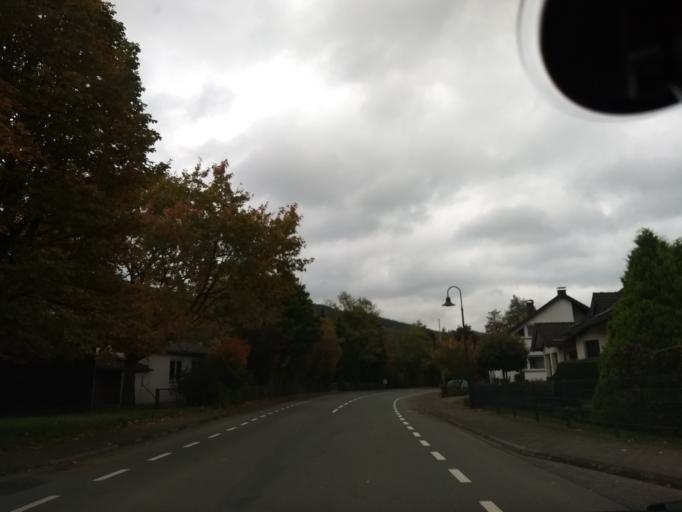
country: DE
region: North Rhine-Westphalia
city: Eslohe
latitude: 51.2524
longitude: 8.1255
